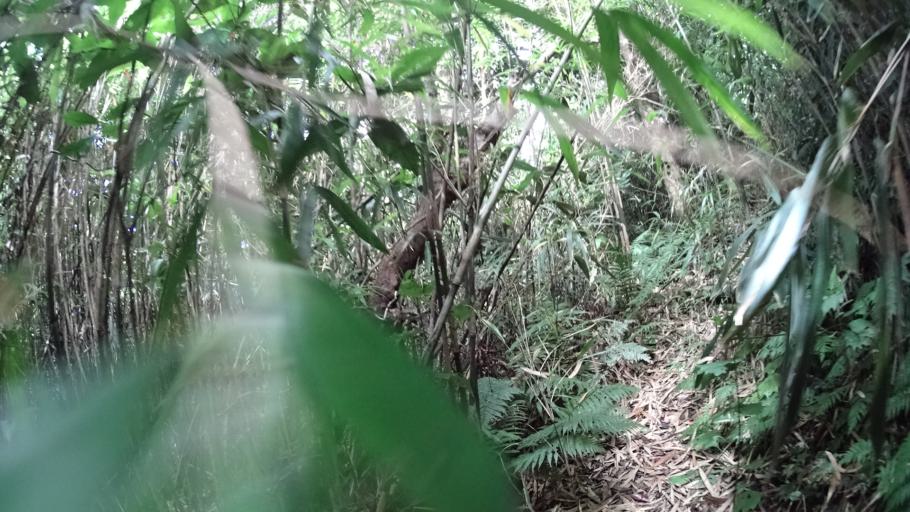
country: JP
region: Shizuoka
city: Shimoda
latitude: 34.5183
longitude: 139.2760
